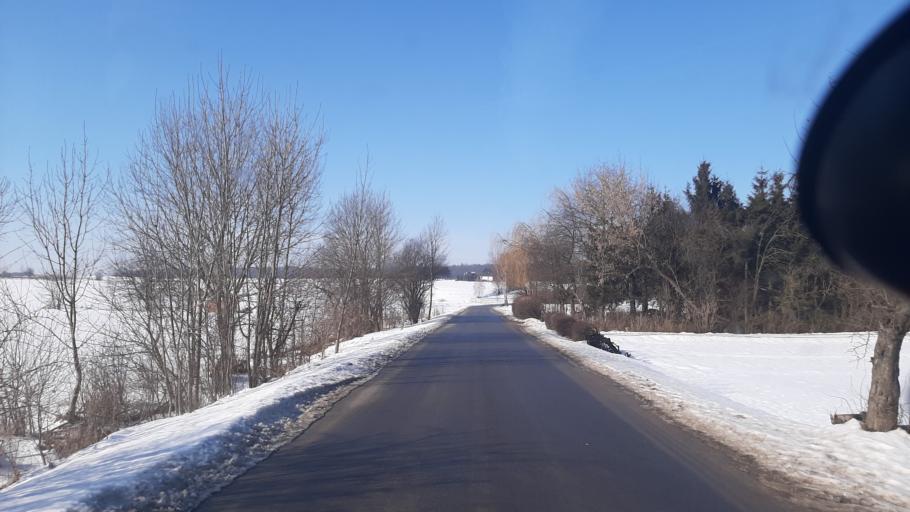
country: PL
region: Lublin Voivodeship
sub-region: Powiat pulawski
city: Naleczow
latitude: 51.2887
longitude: 22.2767
